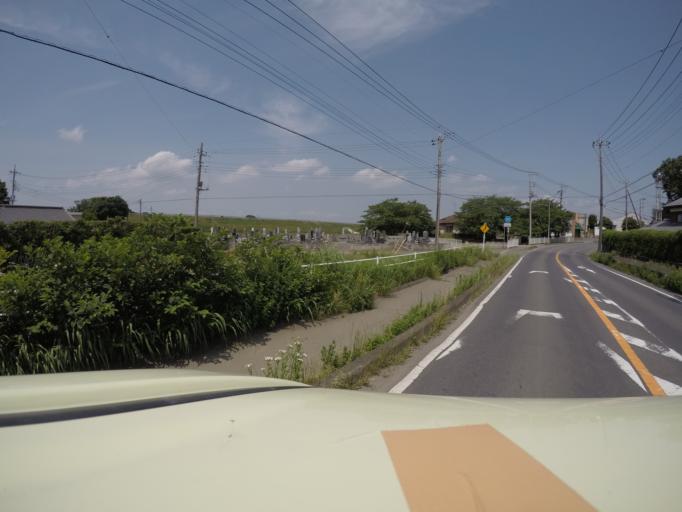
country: JP
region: Ibaraki
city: Iwai
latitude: 36.0698
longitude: 139.9451
